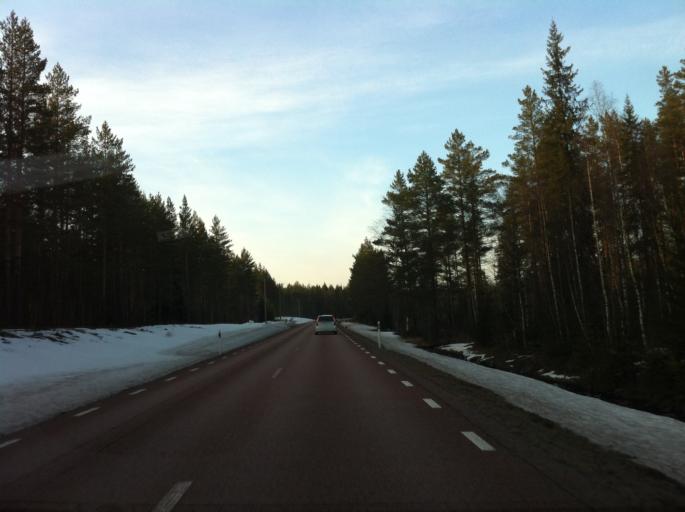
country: SE
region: Vaermland
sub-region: Filipstads Kommun
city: Lesjofors
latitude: 60.1689
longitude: 14.2005
